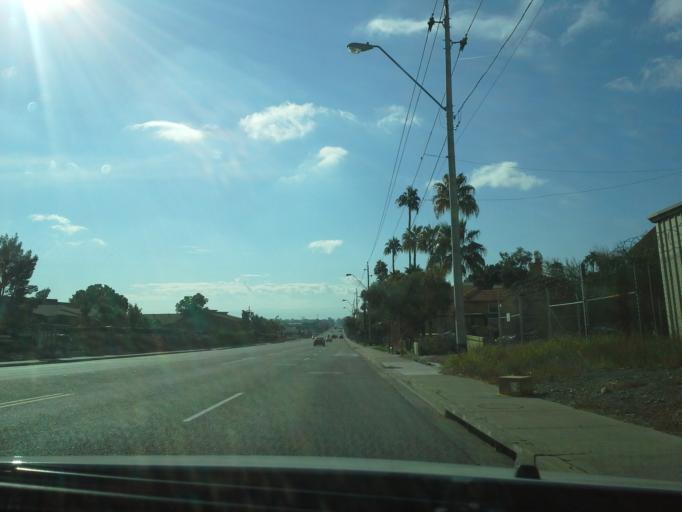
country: US
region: Arizona
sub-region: Maricopa County
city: Glendale
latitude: 33.5789
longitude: -112.0653
